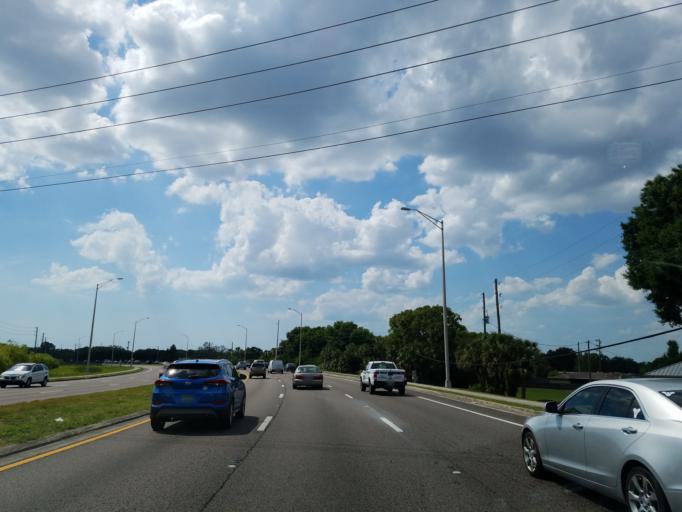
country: US
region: Florida
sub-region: Pasco County
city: Trinity
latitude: 28.2069
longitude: -82.6528
